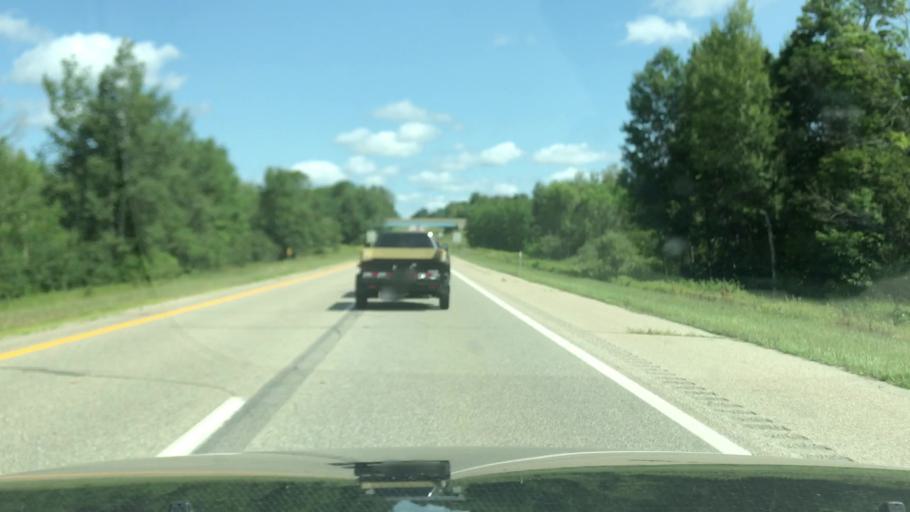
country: US
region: Michigan
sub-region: Mecosta County
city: Big Rapids
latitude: 43.7394
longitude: -85.5313
